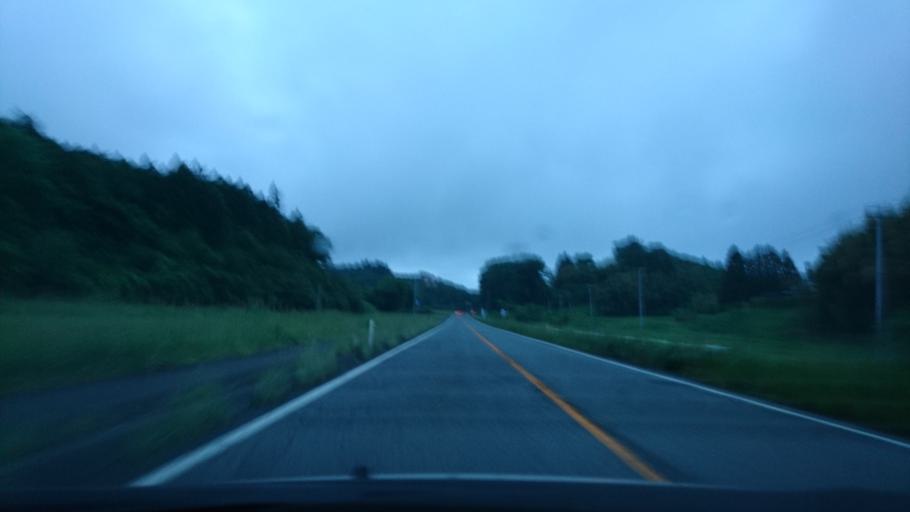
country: JP
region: Iwate
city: Ichinoseki
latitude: 38.8659
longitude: 141.1078
